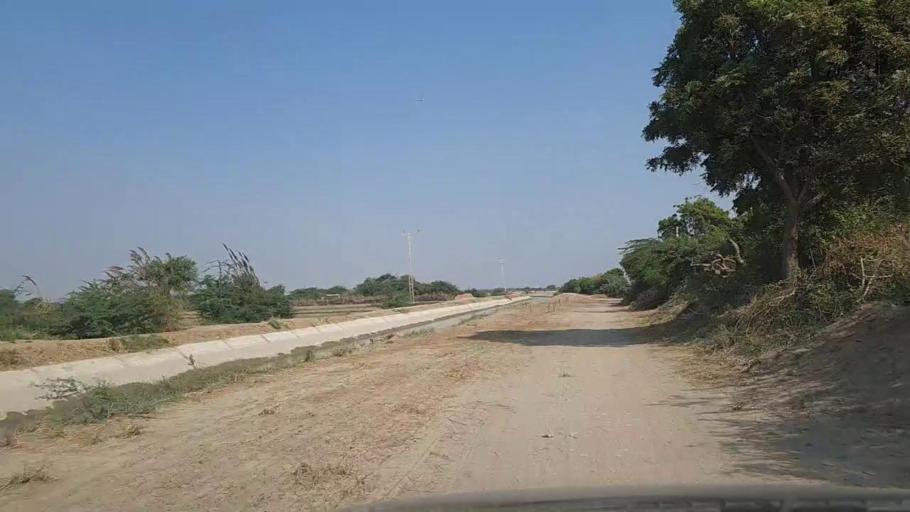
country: PK
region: Sindh
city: Mirpur Sakro
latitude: 24.5231
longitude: 67.8094
